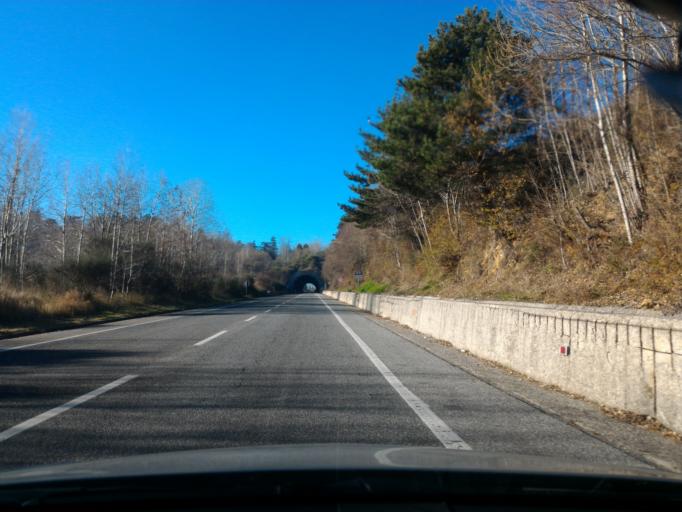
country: IT
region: Calabria
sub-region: Provincia di Cosenza
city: San Giovanni in Fiore
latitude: 39.2663
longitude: 16.7201
